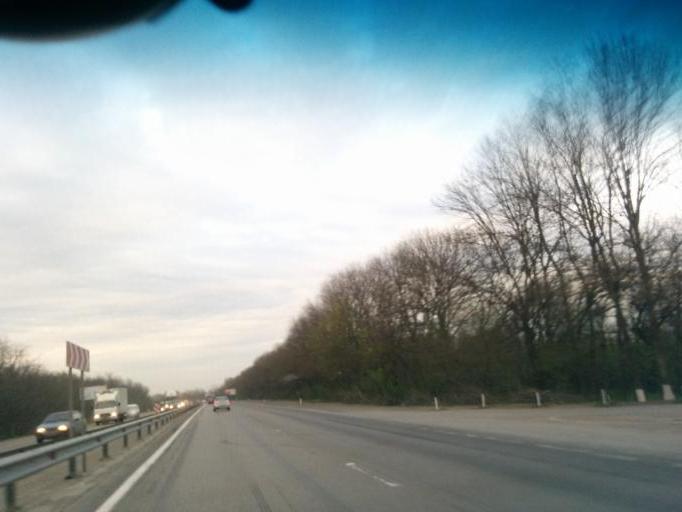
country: RU
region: Rostov
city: Grushevskaya
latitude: 47.3674
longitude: 39.8971
